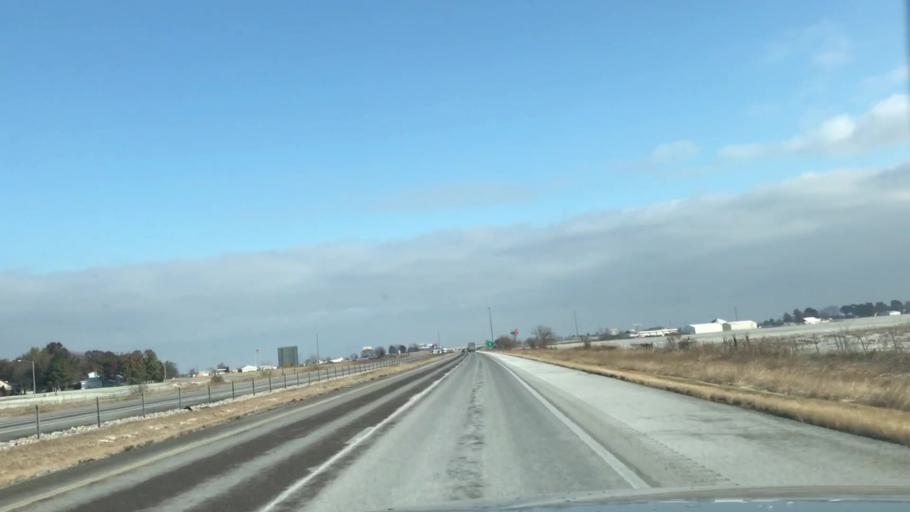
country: US
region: Illinois
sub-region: Madison County
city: Worden
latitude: 38.8807
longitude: -89.8438
